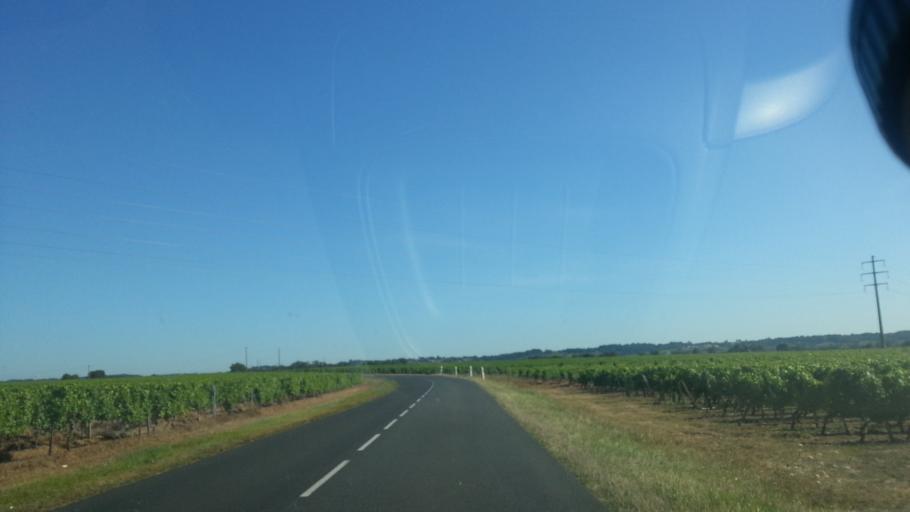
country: FR
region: Aquitaine
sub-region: Departement de la Gironde
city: Podensac
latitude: 44.6359
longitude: -0.3632
